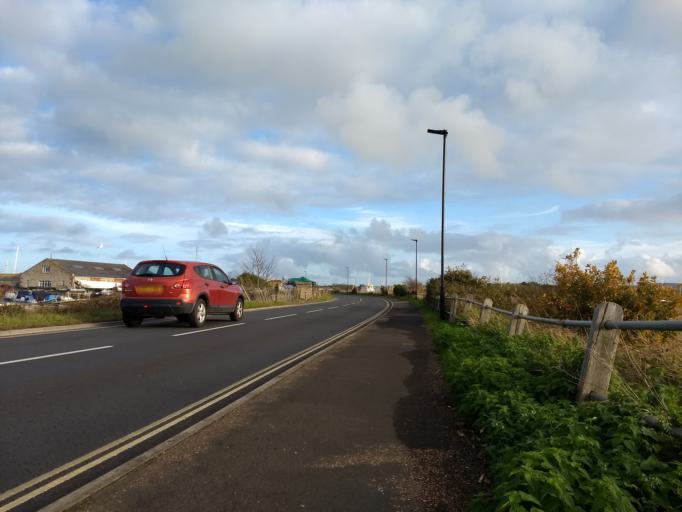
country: GB
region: England
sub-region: Isle of Wight
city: Yarmouth
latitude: 50.7045
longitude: -1.5071
